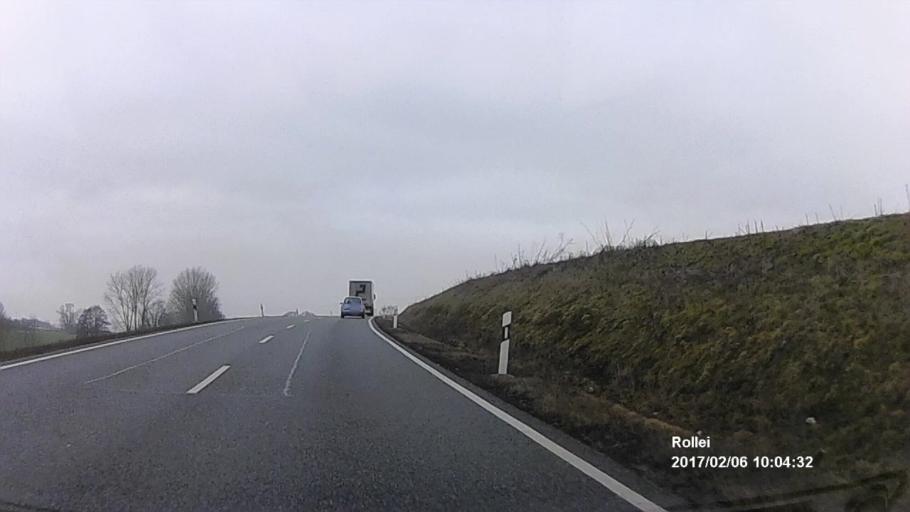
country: DE
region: Thuringia
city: Etzelsrode
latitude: 51.5271
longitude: 10.6292
